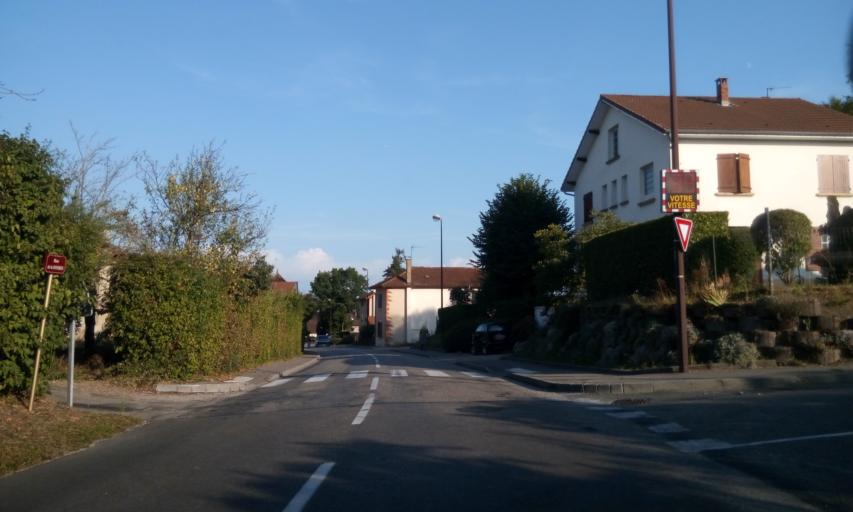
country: FR
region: Rhone-Alpes
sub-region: Departement de l'Ain
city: Chalamont
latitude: 45.9983
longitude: 5.1658
